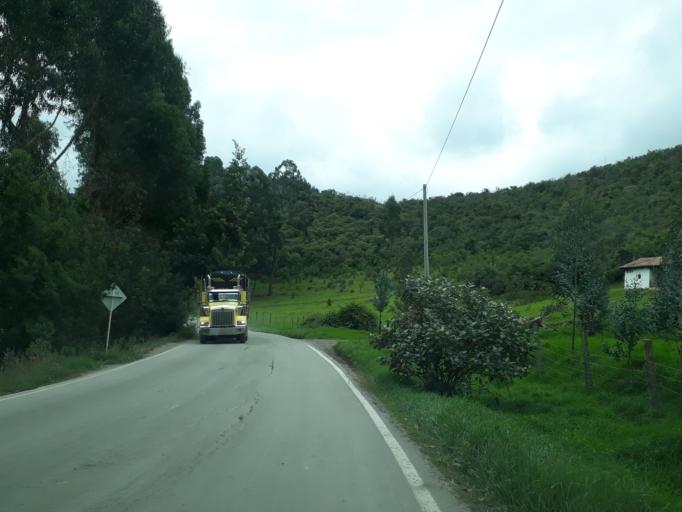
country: CO
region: Cundinamarca
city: Ubate
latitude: 5.3222
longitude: -73.7797
